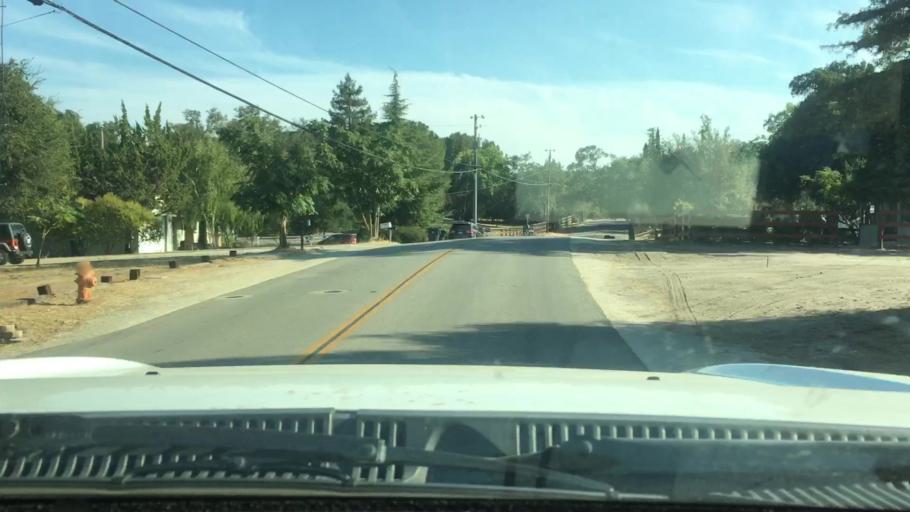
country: US
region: California
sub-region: San Luis Obispo County
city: Atascadero
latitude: 35.4596
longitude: -120.6539
